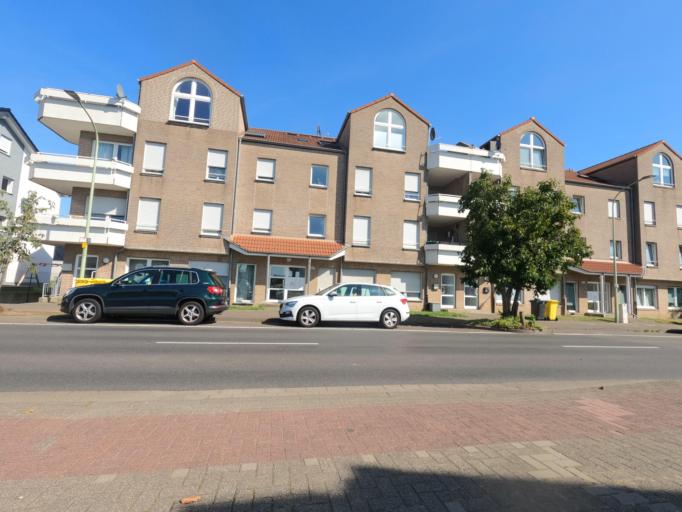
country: DE
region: North Rhine-Westphalia
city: Baesweiler
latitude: 50.9087
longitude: 6.1733
